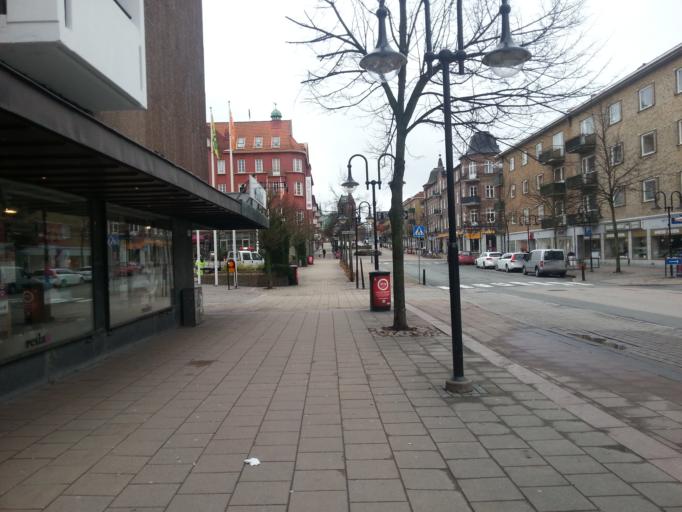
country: SE
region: Skane
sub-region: Hassleholms Kommun
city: Hassleholm
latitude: 56.1578
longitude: 13.7643
